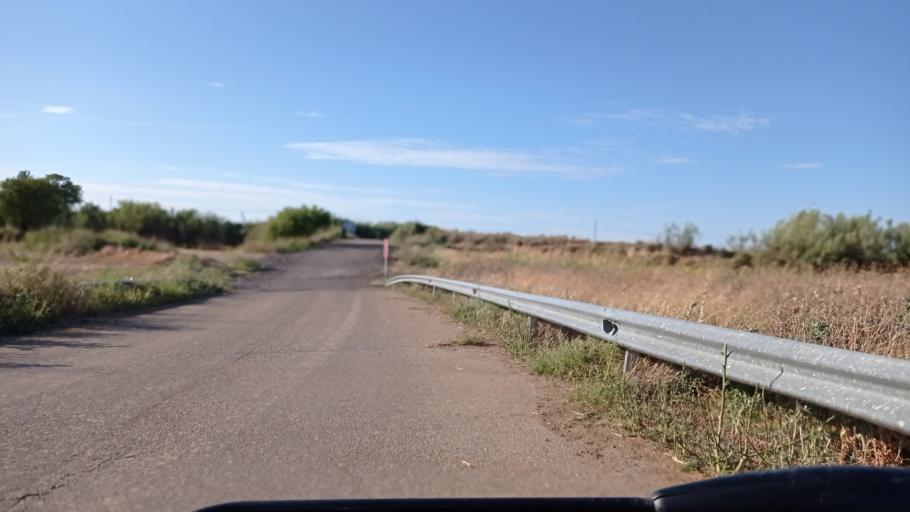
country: ES
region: Aragon
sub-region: Provincia de Zaragoza
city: Oliver-Valdefierro, Oliver, Valdefierro
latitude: 41.6620
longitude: -0.9499
